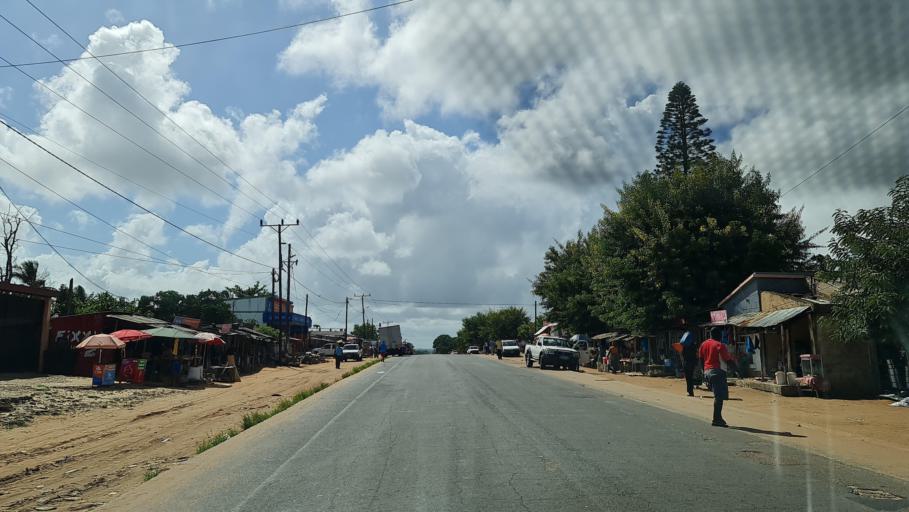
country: MZ
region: Gaza
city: Manjacaze
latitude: -24.6742
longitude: 34.5779
